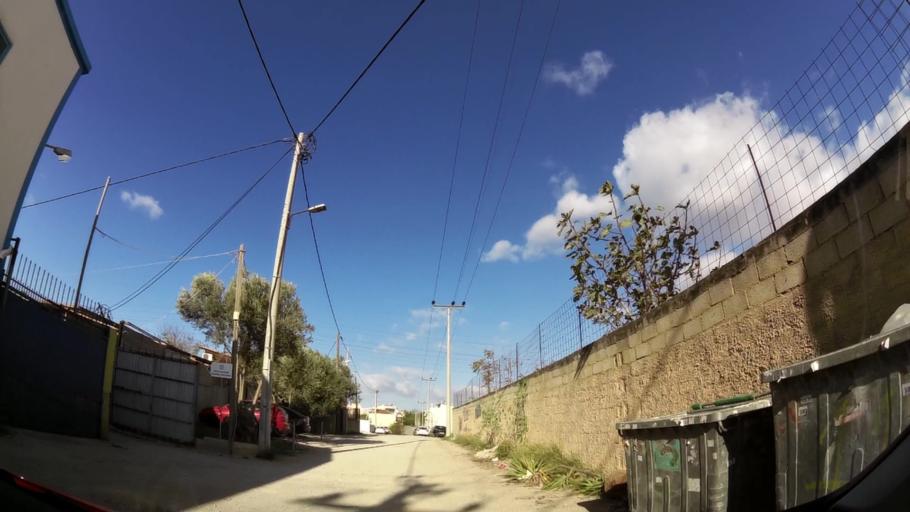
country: GR
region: Attica
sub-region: Nomarchia Athinas
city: Metamorfosi
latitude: 38.0665
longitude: 23.7459
